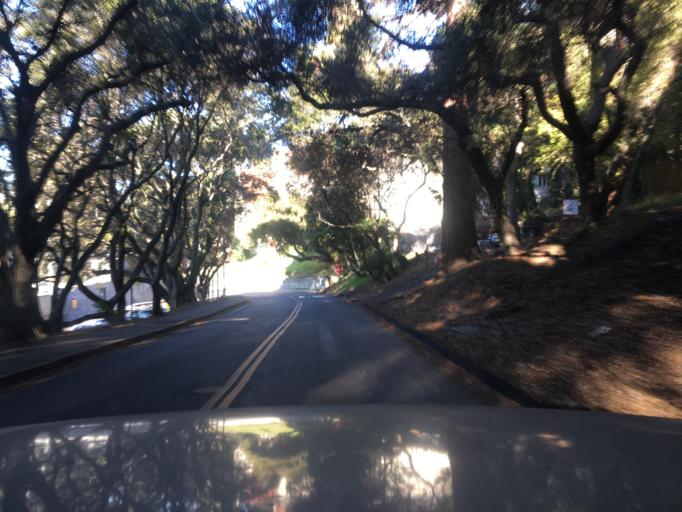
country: US
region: California
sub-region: Alameda County
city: Berkeley
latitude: 37.8726
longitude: -122.2521
